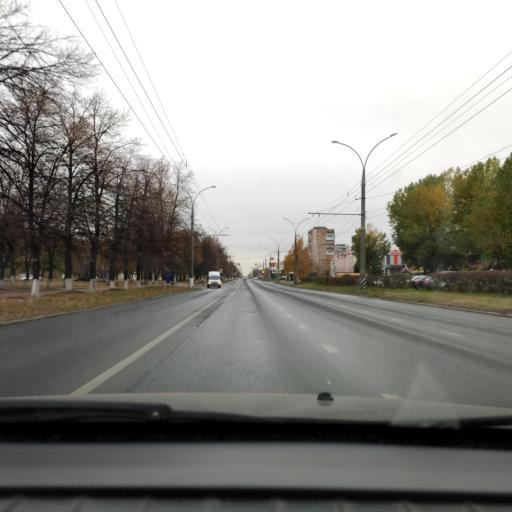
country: RU
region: Samara
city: Tol'yatti
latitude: 53.5322
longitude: 49.2770
